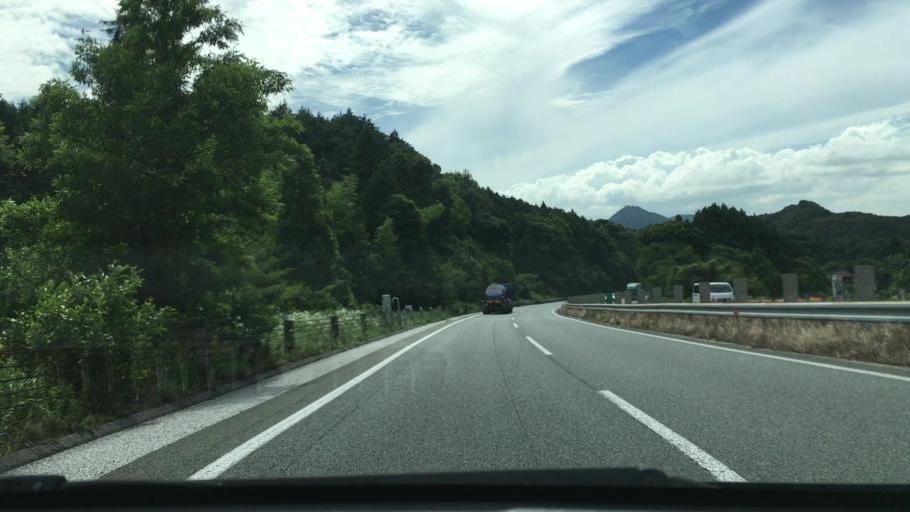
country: JP
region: Yamaguchi
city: Ogori-shimogo
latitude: 34.1438
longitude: 131.3522
